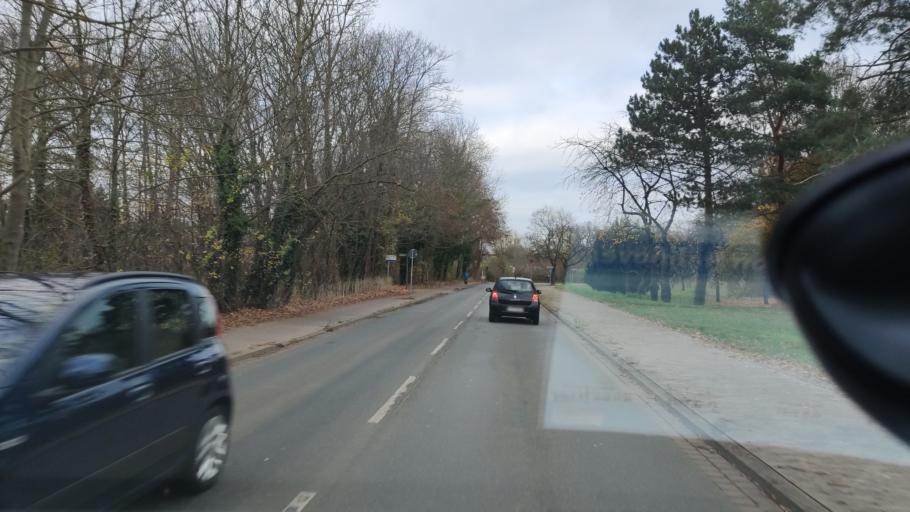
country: DE
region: Lower Saxony
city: Hemmingen
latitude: 52.3331
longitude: 9.7559
